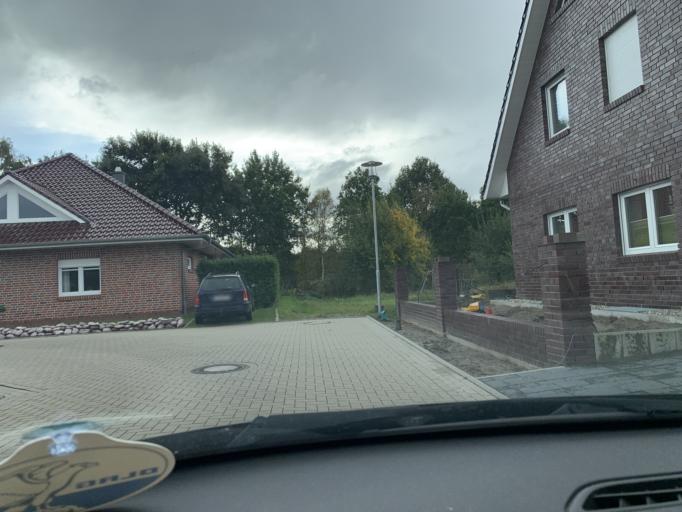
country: DE
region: Lower Saxony
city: Apen
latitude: 53.2269
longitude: 7.7711
